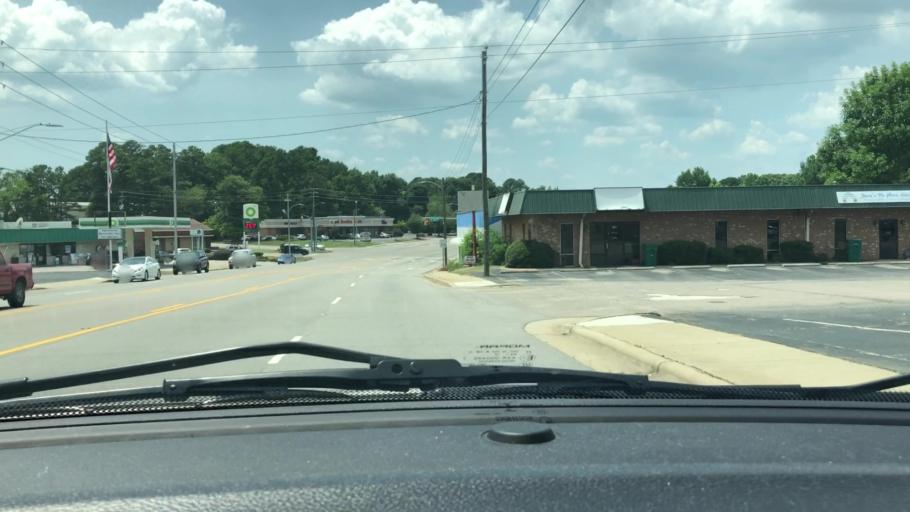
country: US
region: North Carolina
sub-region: Lee County
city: Sanford
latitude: 35.4708
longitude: -79.1709
